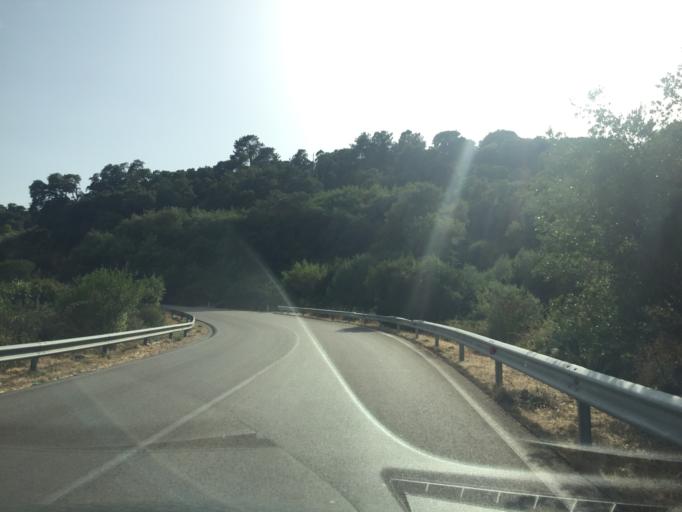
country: IT
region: Sardinia
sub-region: Provincia di Olbia-Tempio
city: Luras
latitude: 40.9333
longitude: 9.1830
